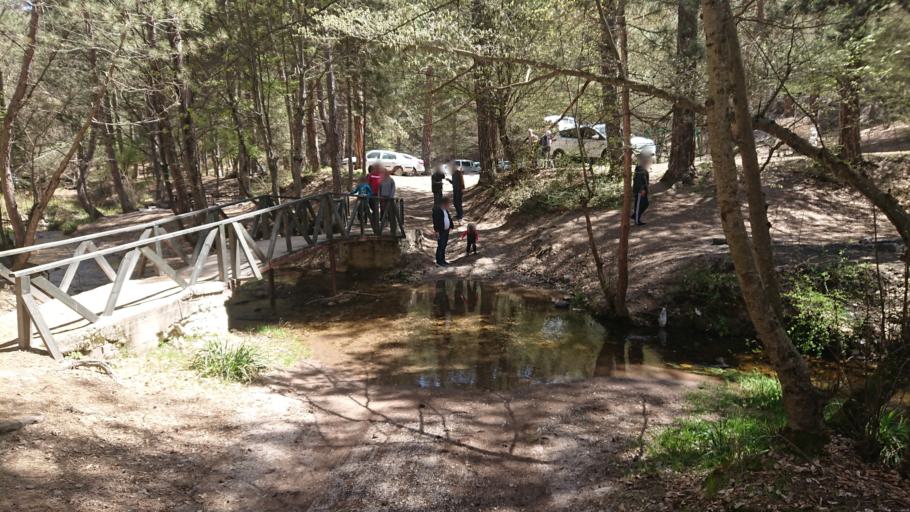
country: TR
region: Kuetahya
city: Sabuncu
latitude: 39.5102
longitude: 30.4221
